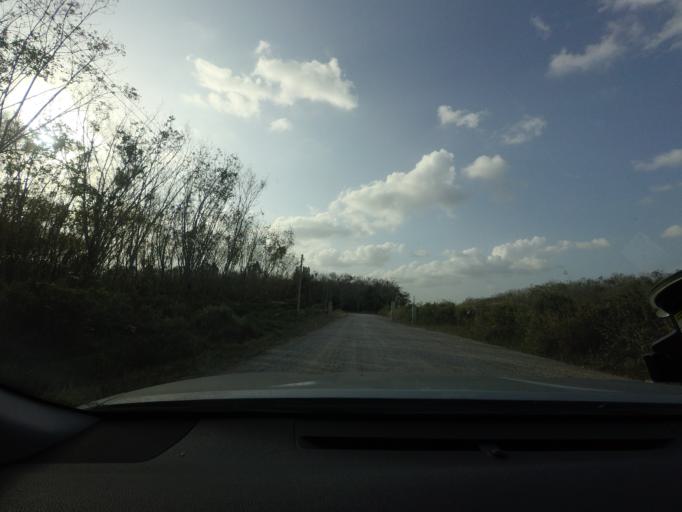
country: TH
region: Pattani
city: Mae Lan
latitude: 6.6211
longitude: 101.2500
